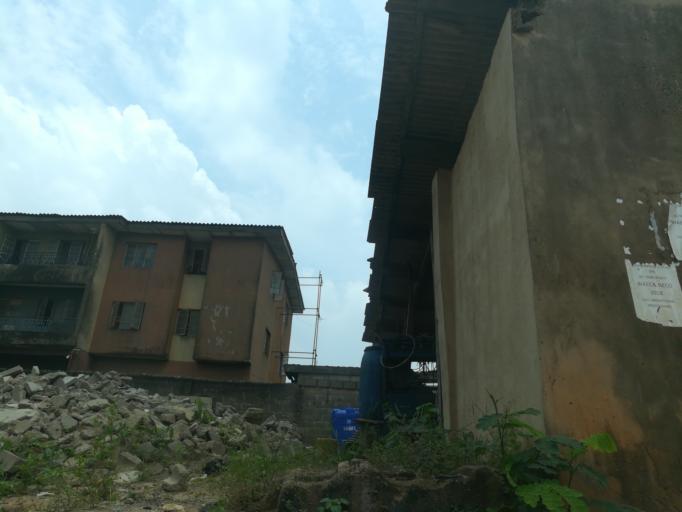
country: NG
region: Lagos
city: Ikorodu
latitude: 6.6258
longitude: 3.5283
